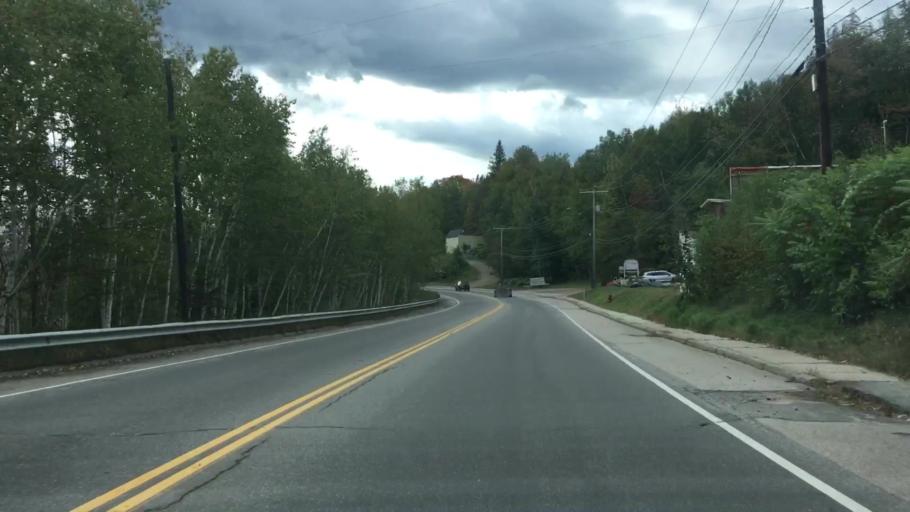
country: US
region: New Hampshire
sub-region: Coos County
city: Berlin
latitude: 44.4531
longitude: -71.1887
